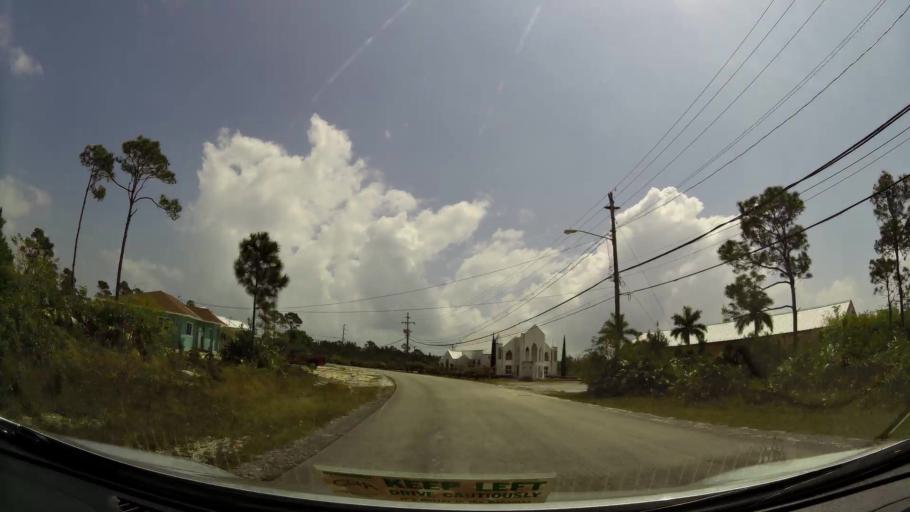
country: BS
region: Freeport
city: Lucaya
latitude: 26.5249
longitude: -78.6315
